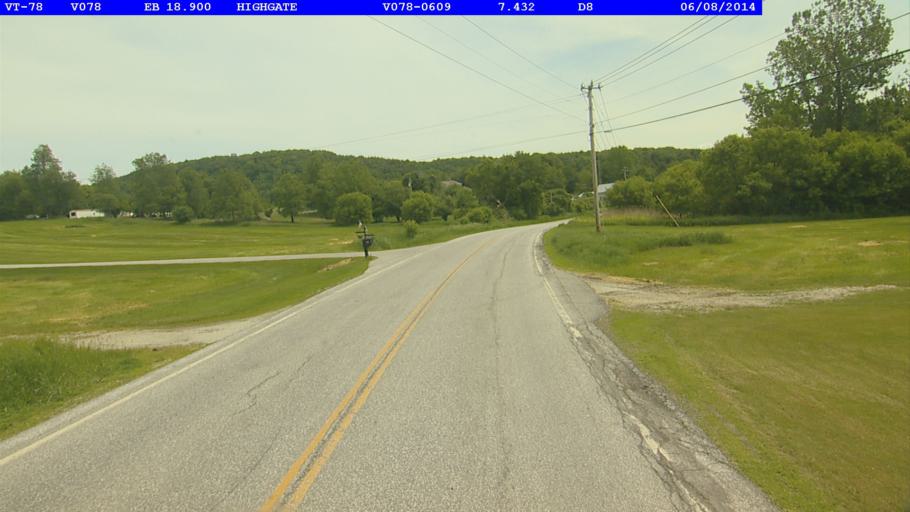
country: US
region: Vermont
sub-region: Franklin County
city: Swanton
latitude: 44.9267
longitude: -72.9727
